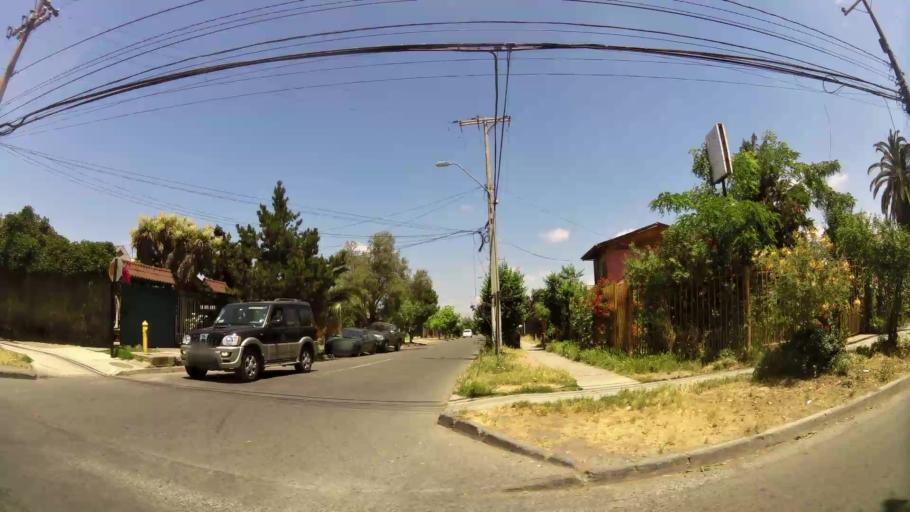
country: CL
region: Santiago Metropolitan
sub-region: Provincia de Talagante
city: Penaflor
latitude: -33.5667
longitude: -70.7950
